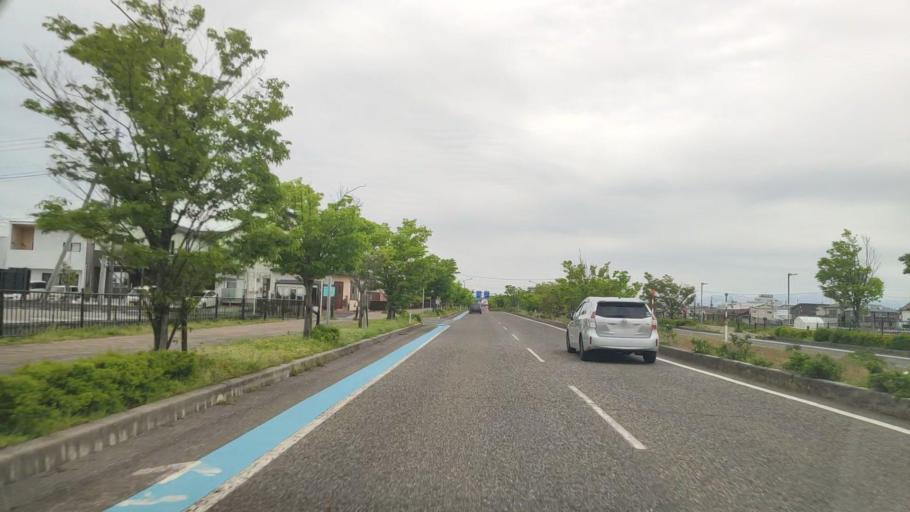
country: JP
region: Niigata
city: Kameda-honcho
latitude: 37.8839
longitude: 139.0690
